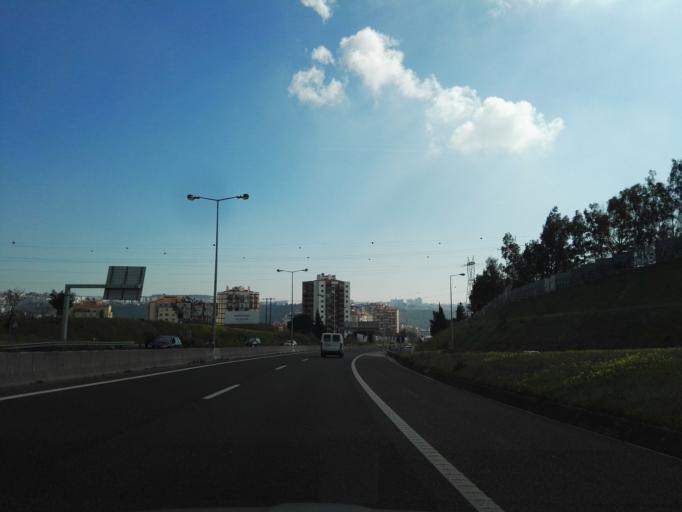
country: PT
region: Lisbon
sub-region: Odivelas
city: Povoa de Santo Adriao
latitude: 38.8011
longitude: -9.1770
